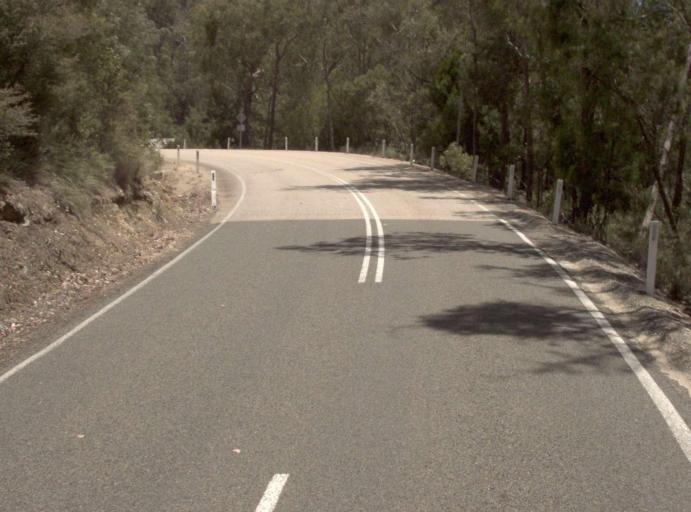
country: AU
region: Victoria
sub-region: East Gippsland
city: Lakes Entrance
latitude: -37.5687
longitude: 147.8899
